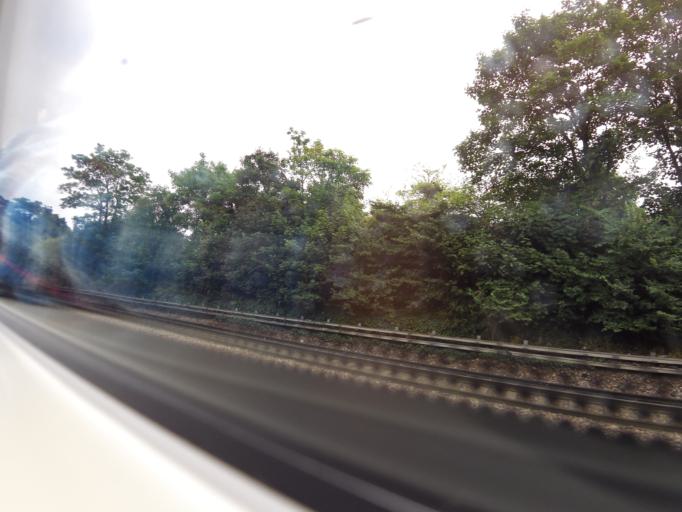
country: GB
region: England
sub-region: Greater London
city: Beckenham
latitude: 51.4290
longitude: -0.0538
